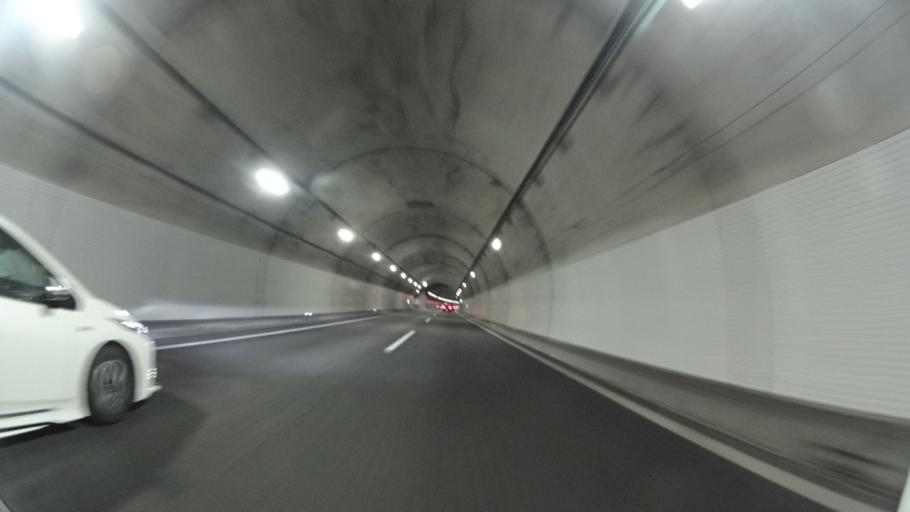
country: JP
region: Ehime
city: Saijo
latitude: 33.8944
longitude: 133.1985
